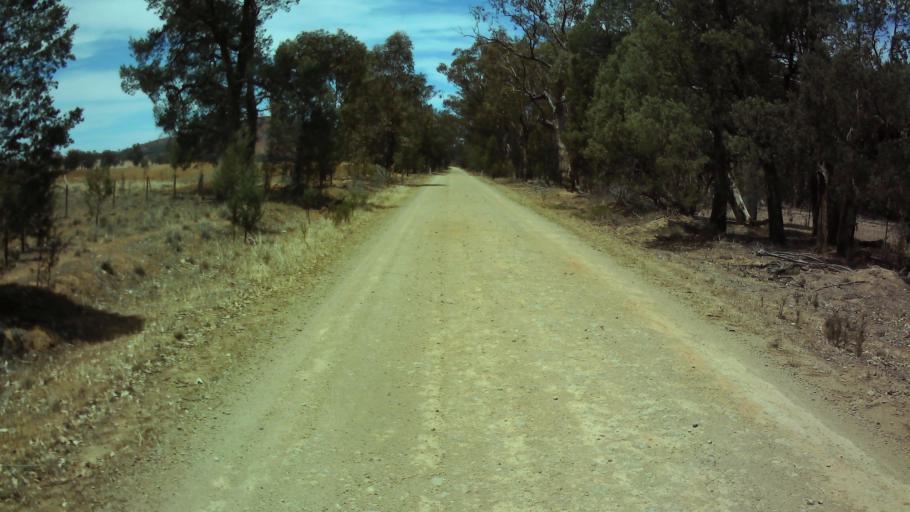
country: AU
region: New South Wales
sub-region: Weddin
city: Grenfell
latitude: -33.7615
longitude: 148.1228
